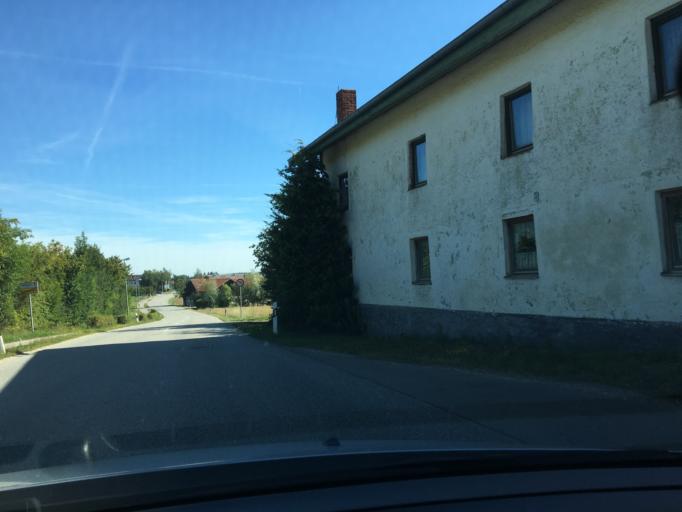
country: DE
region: Bavaria
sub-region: Lower Bavaria
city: Bodenkirchen
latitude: 48.3882
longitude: 12.3885
